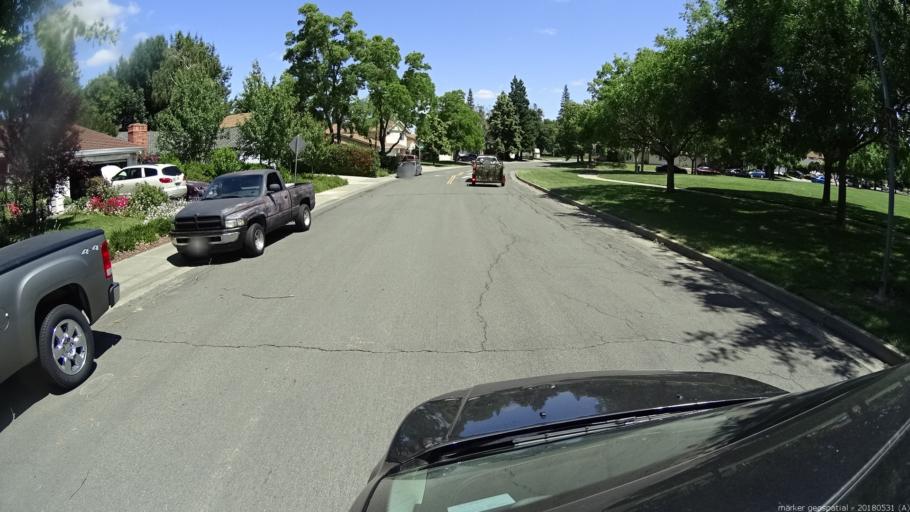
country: US
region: California
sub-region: Sacramento County
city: Sacramento
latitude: 38.6231
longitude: -121.5073
